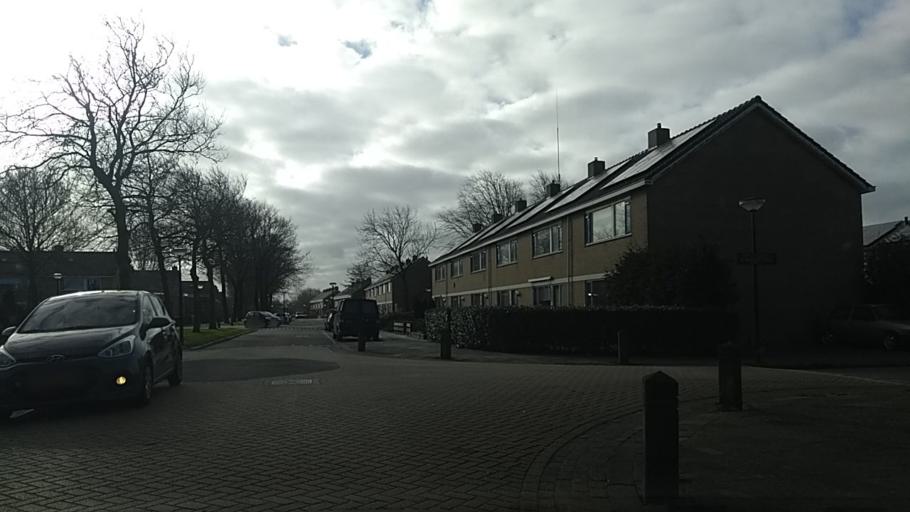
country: NL
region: Friesland
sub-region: Gemeente Harlingen
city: Harlingen
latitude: 53.1664
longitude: 5.4387
